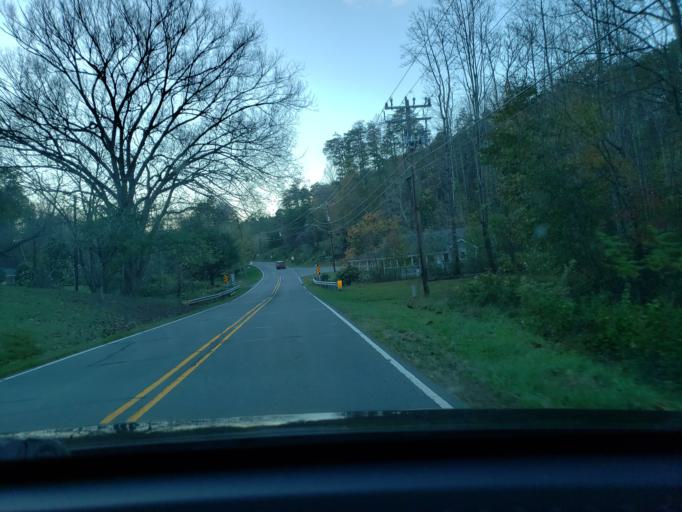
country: US
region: North Carolina
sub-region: Stokes County
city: Danbury
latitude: 36.4106
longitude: -80.2127
